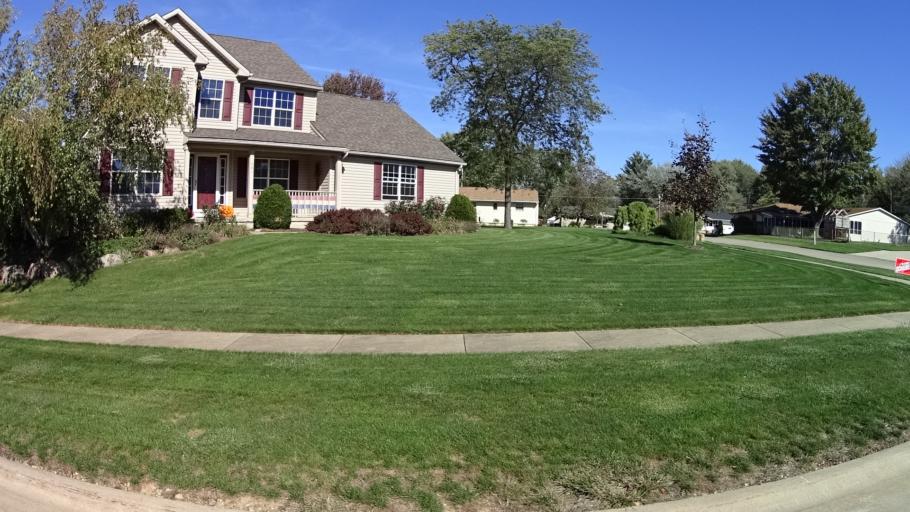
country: US
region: Ohio
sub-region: Lorain County
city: Amherst
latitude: 41.3875
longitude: -82.2199
